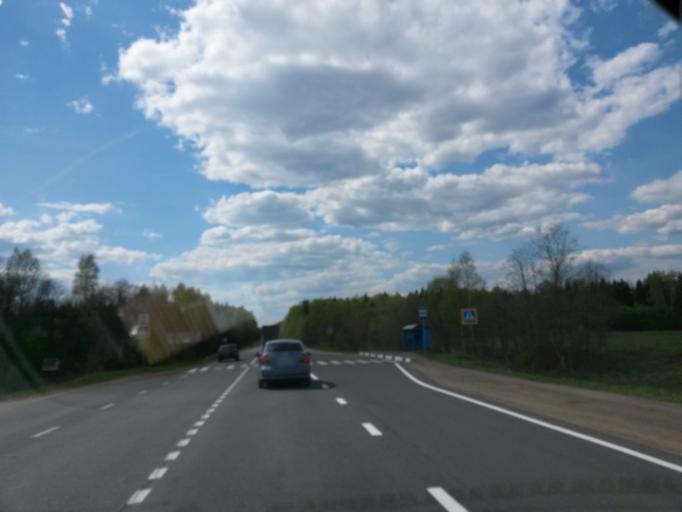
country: RU
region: Jaroslavl
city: Bol'shoye Selo
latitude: 57.7229
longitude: 38.8813
